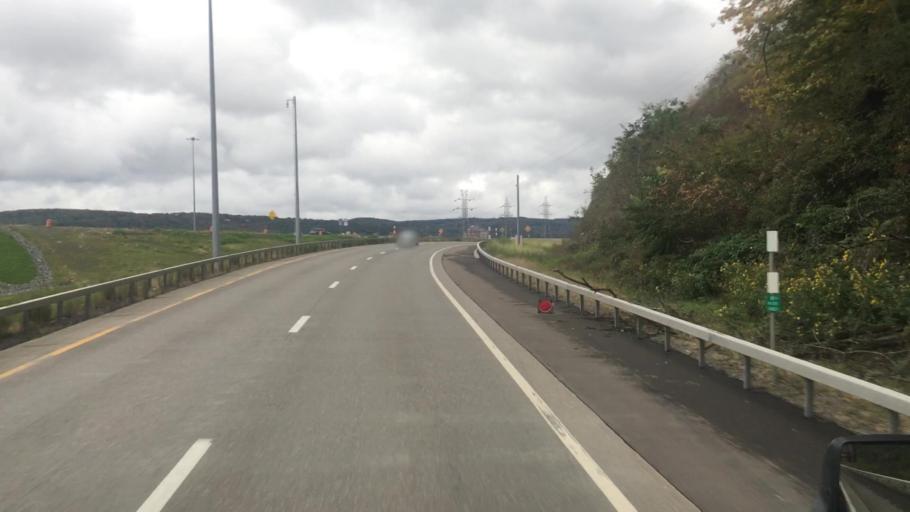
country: US
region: New York
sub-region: Broome County
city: Binghamton
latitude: 42.1155
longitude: -75.9104
